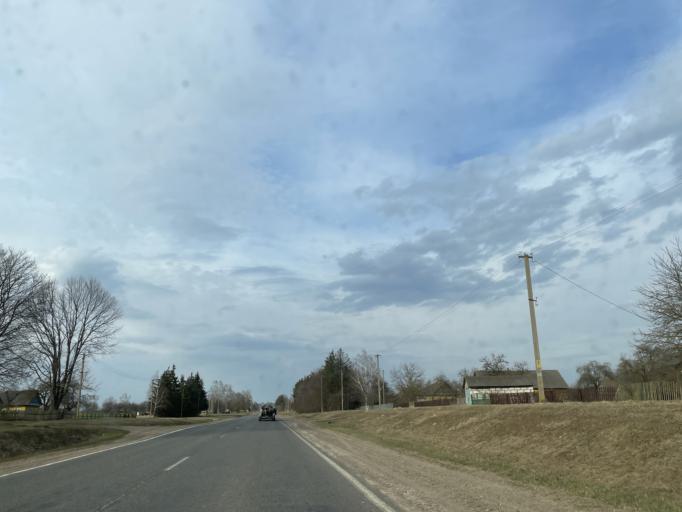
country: BY
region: Minsk
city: Klyetsk
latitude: 53.1187
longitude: 26.6644
